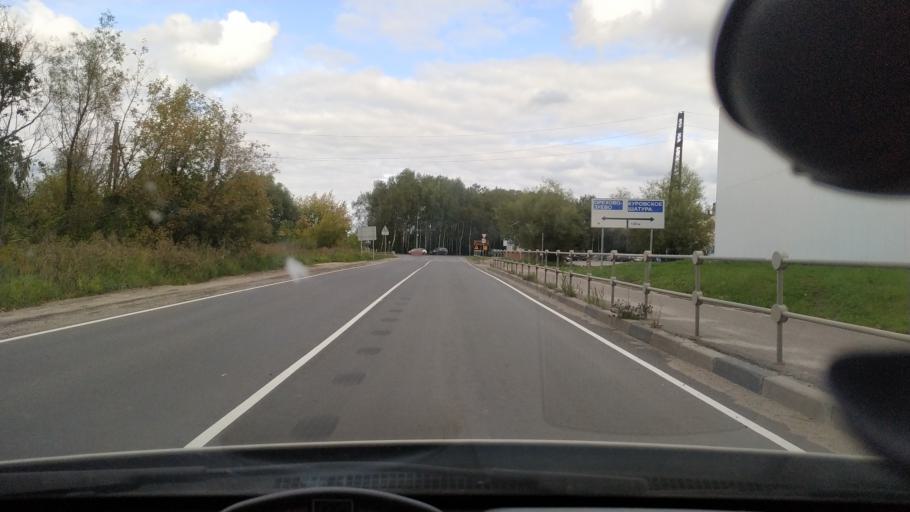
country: RU
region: Moskovskaya
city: Kabanovo
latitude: 55.7387
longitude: 38.9414
